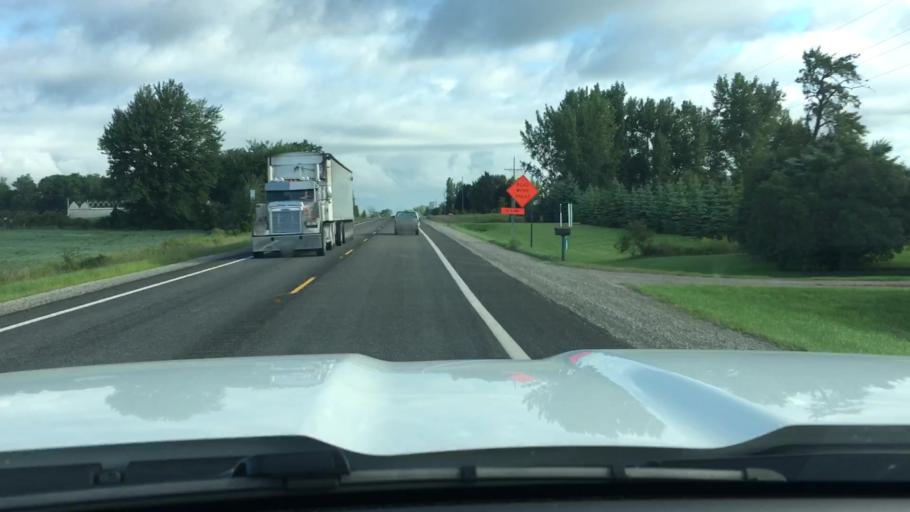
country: US
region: Michigan
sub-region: Tuscola County
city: Caro
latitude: 43.3970
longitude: -83.3835
